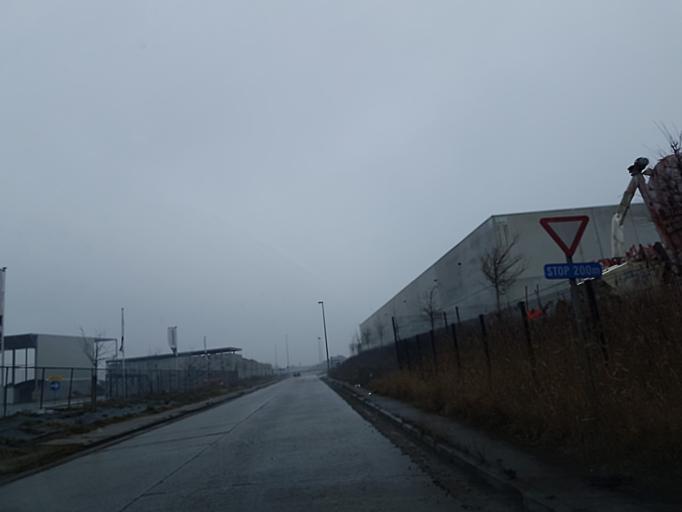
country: BE
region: Flanders
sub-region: Provincie West-Vlaanderen
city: Bredene
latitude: 51.2134
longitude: 2.9796
